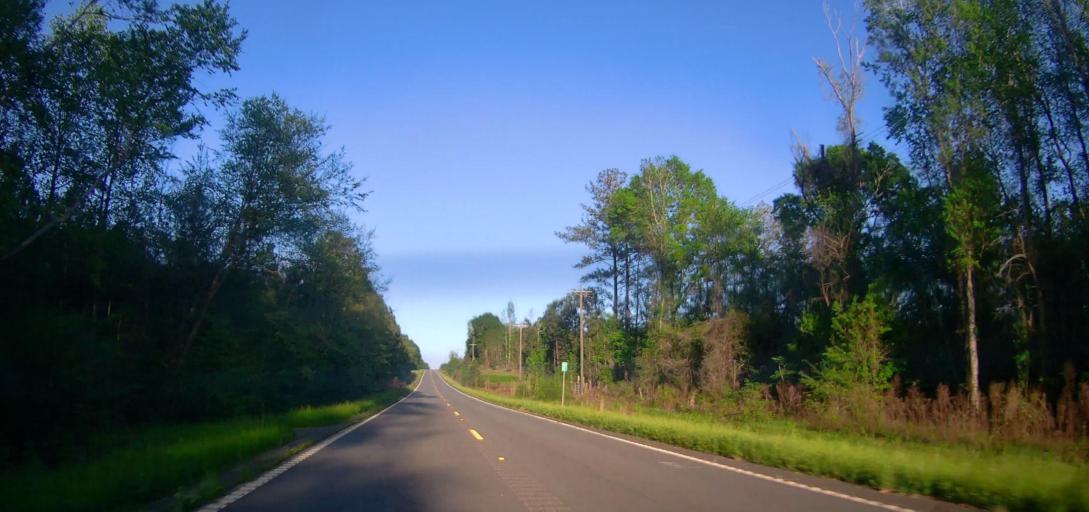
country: US
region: Georgia
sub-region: Schley County
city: Ellaville
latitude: 32.3208
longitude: -84.2855
